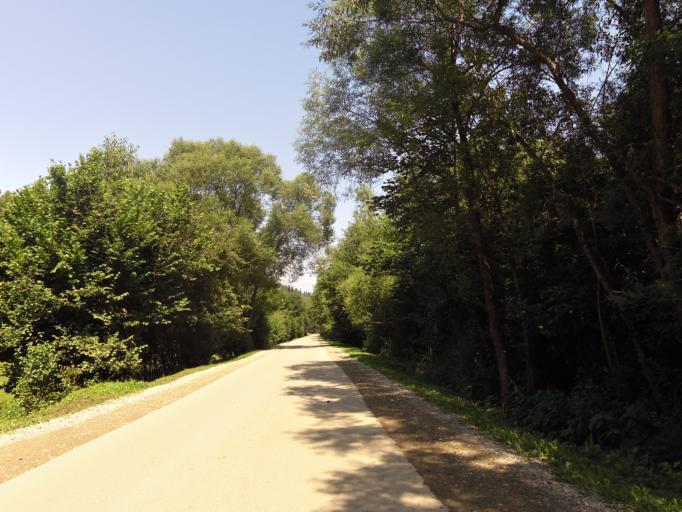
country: PL
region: Silesian Voivodeship
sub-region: Powiat zywiecki
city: Cisiec
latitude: 49.5971
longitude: 19.1002
